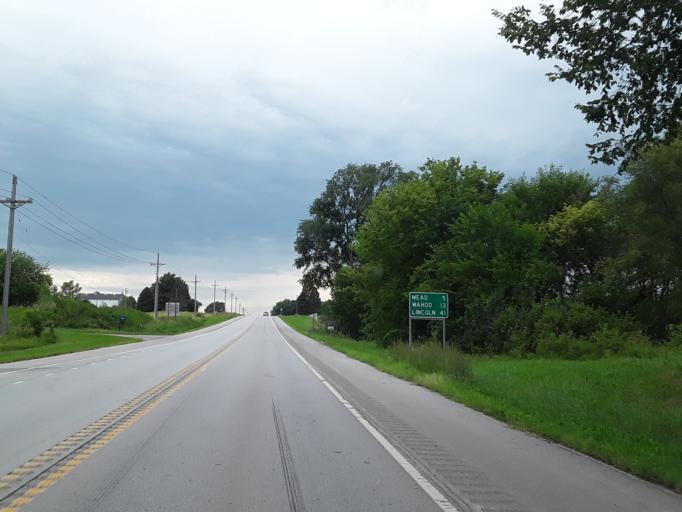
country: US
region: Nebraska
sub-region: Saunders County
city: Yutan
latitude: 41.2338
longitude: -96.4001
